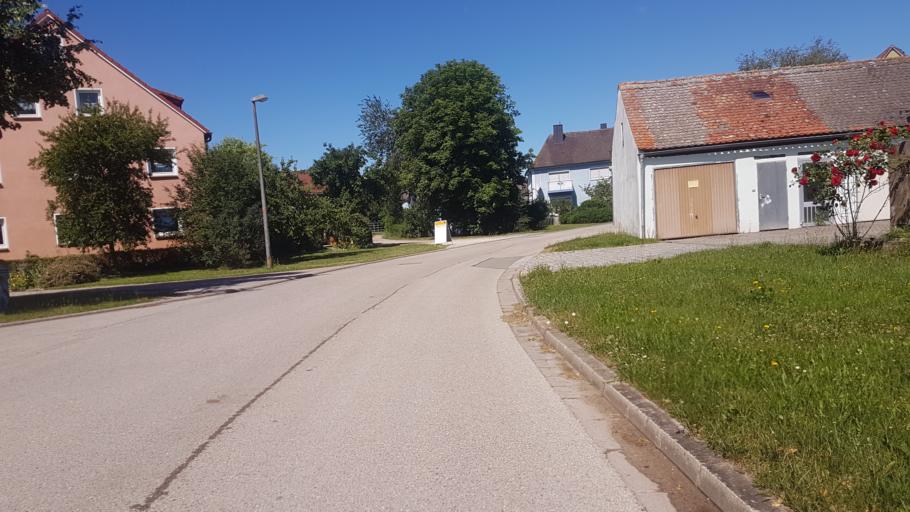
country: DE
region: Bavaria
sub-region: Regierungsbezirk Mittelfranken
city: Herrieden
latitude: 49.2201
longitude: 10.5243
